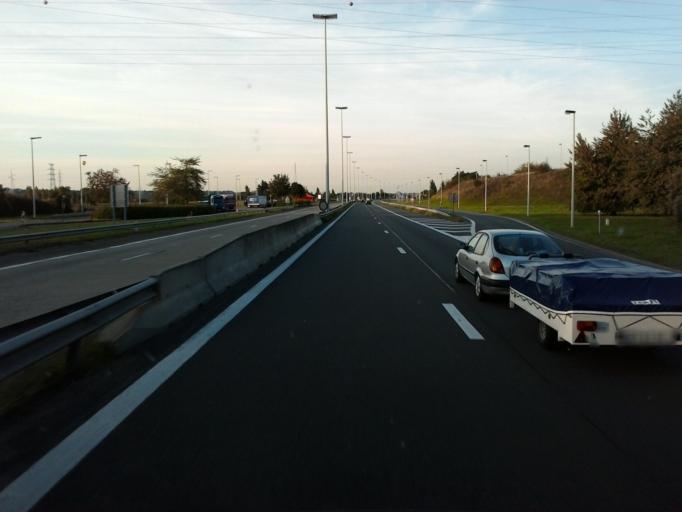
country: BE
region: Wallonia
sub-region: Province de Liege
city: Vise
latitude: 50.7453
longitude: 5.6927
